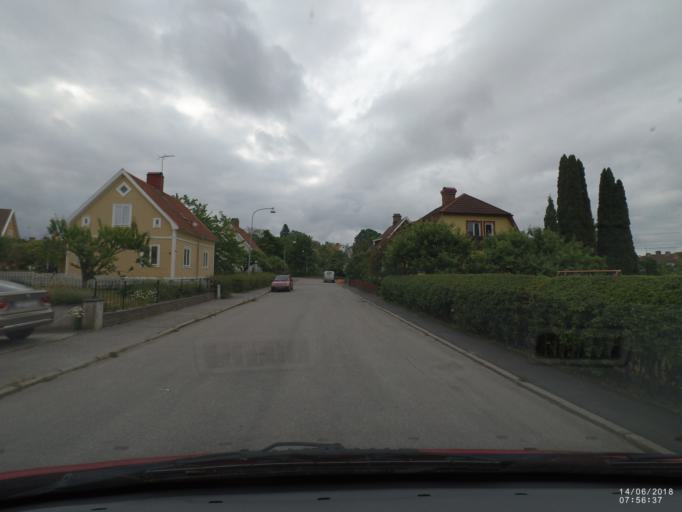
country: SE
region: Soedermanland
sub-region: Nykopings Kommun
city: Nykoping
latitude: 58.7584
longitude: 17.0196
